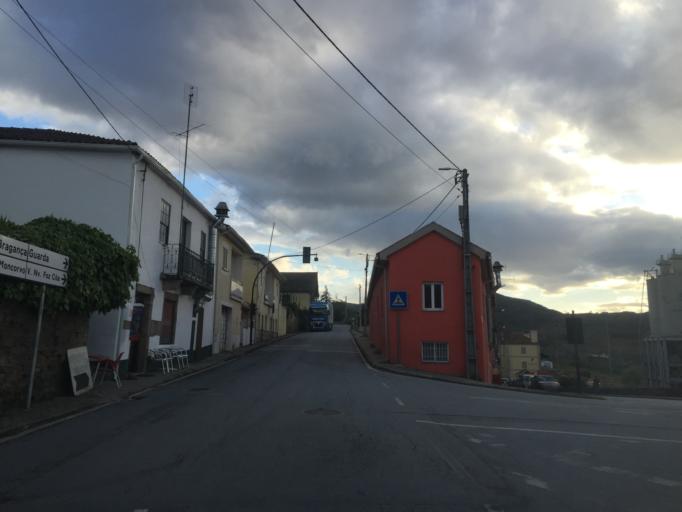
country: PT
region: Braganca
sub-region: Torre de Moncorvo
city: Torre de Moncorvo
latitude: 41.1309
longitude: -7.1214
